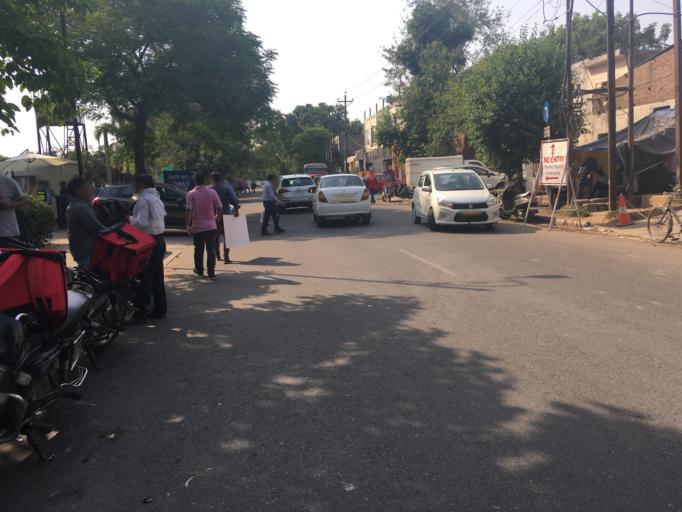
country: IN
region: Chandigarh
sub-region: Chandigarh
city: Chandigarh
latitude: 30.7060
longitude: 76.8018
